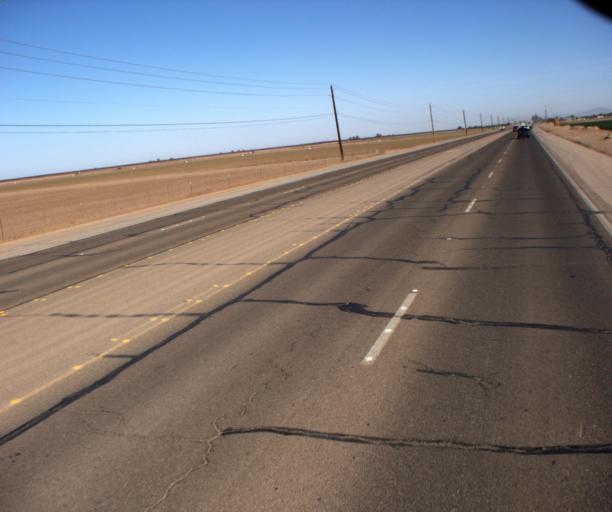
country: US
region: Arizona
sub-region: Yuma County
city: San Luis
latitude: 32.5332
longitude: -114.7867
